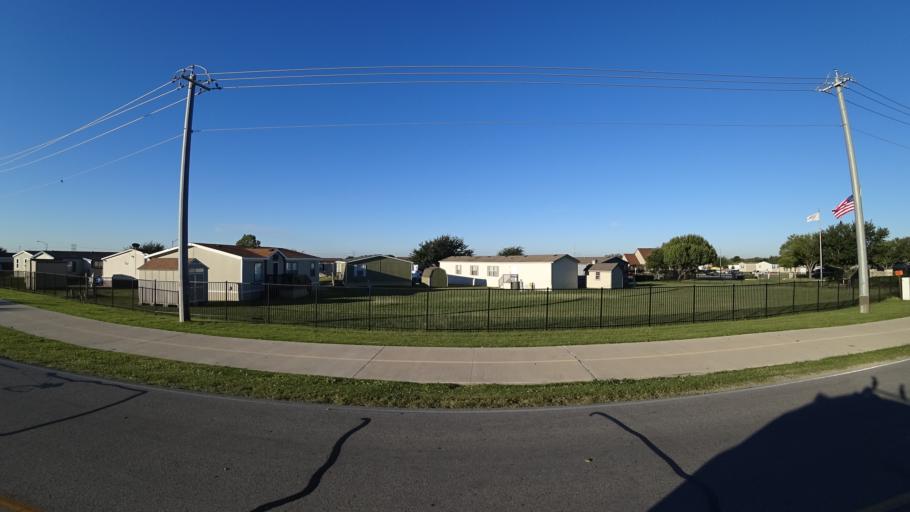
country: US
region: Texas
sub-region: Travis County
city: Manor
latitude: 30.3165
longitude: -97.6231
